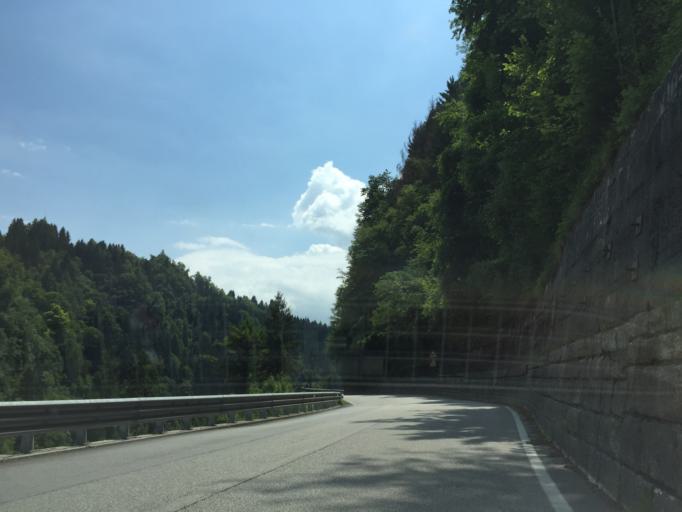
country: IT
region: Veneto
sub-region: Provincia di Belluno
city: Lamon
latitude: 46.0541
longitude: 11.7629
